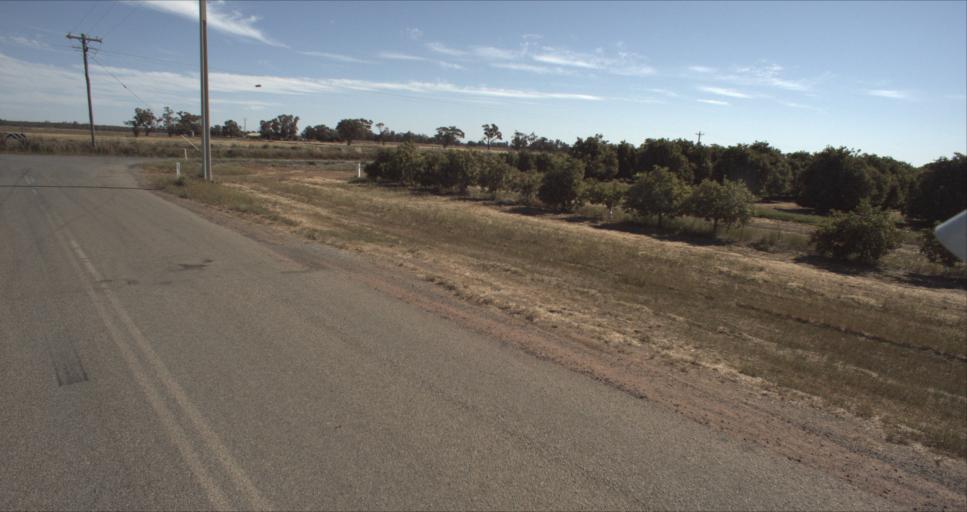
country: AU
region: New South Wales
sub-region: Leeton
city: Leeton
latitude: -34.5874
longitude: 146.3787
